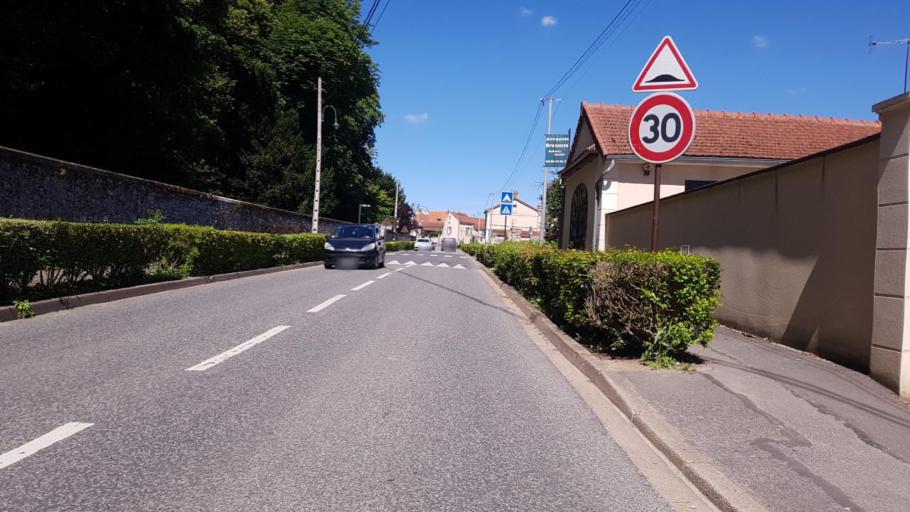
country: FR
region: Ile-de-France
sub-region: Departement de Seine-et-Marne
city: Saacy-sur-Marne
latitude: 48.9712
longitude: 3.1901
